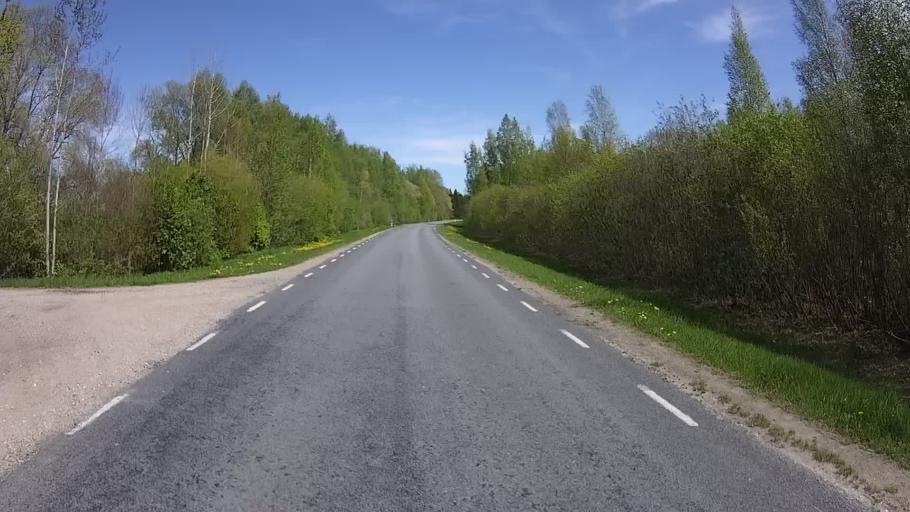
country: LV
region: Apes Novads
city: Ape
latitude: 57.6052
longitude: 26.5330
